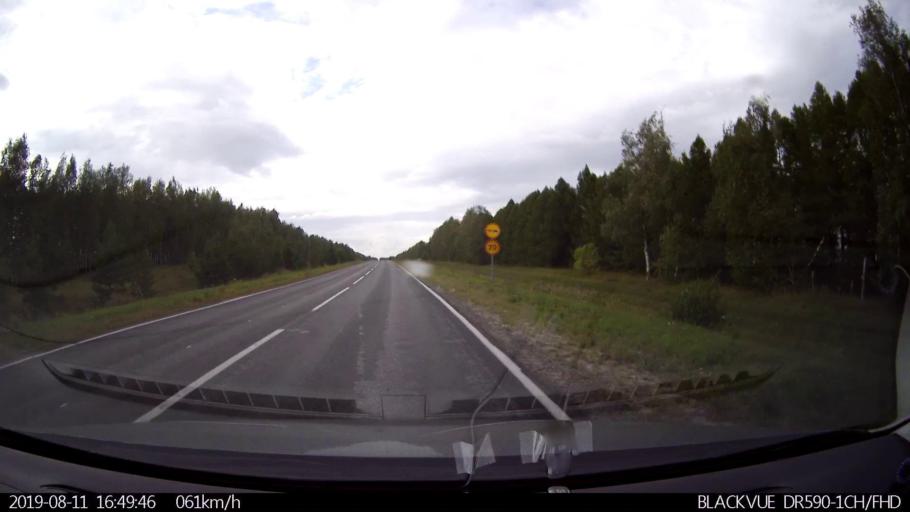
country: RU
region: Ulyanovsk
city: Mayna
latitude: 54.2233
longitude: 47.6947
